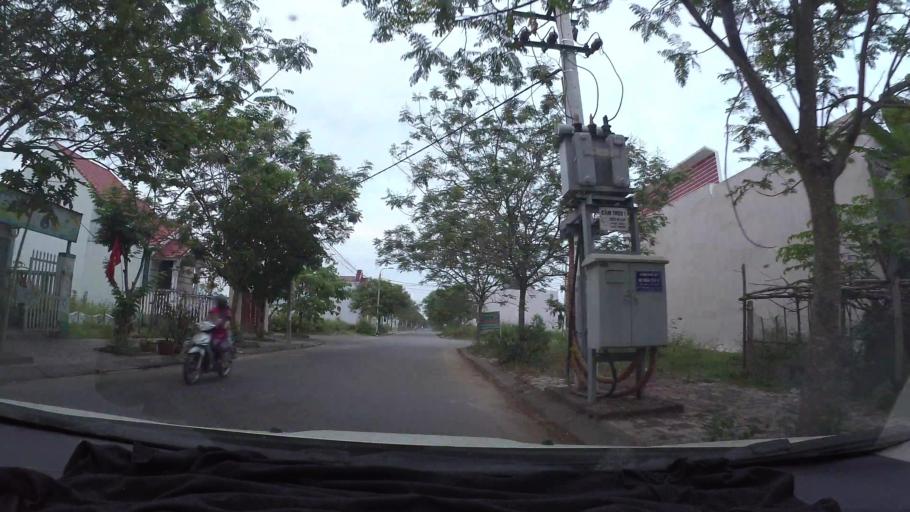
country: VN
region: Da Nang
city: Lien Chieu
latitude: 16.0712
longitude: 108.1066
